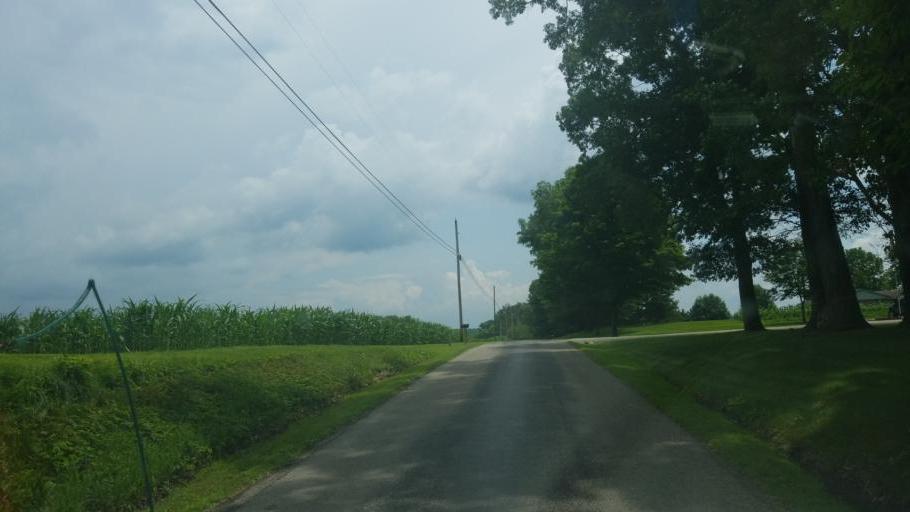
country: US
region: Ohio
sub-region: Wayne County
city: West Salem
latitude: 40.8358
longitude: -82.1147
